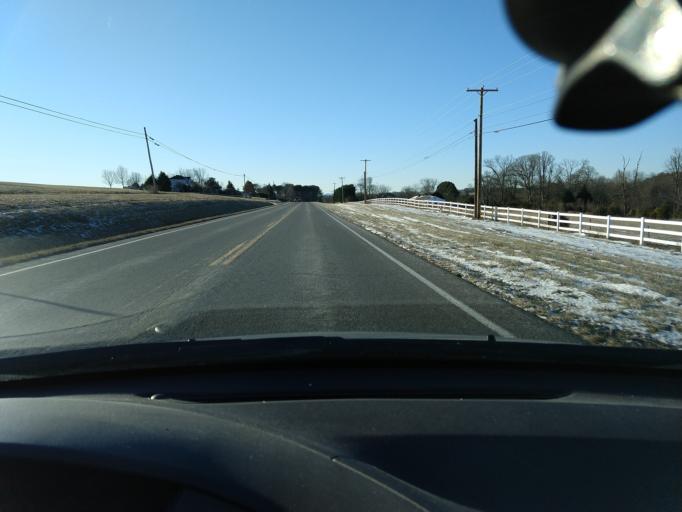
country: US
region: Virginia
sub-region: City of Bedford
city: Bedford
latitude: 37.3053
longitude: -79.5362
